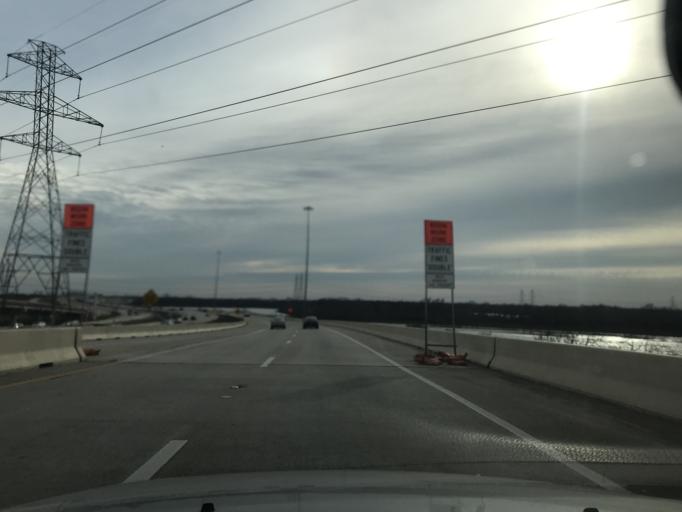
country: US
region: Texas
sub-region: Dallas County
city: Carrollton
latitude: 32.9811
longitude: -96.9333
